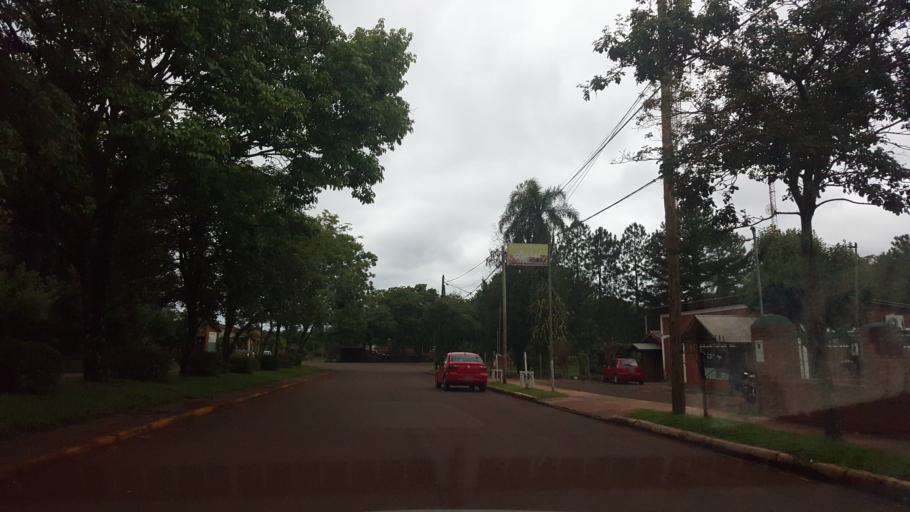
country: AR
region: Misiones
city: Ruiz de Montoya
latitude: -26.9688
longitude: -55.0538
